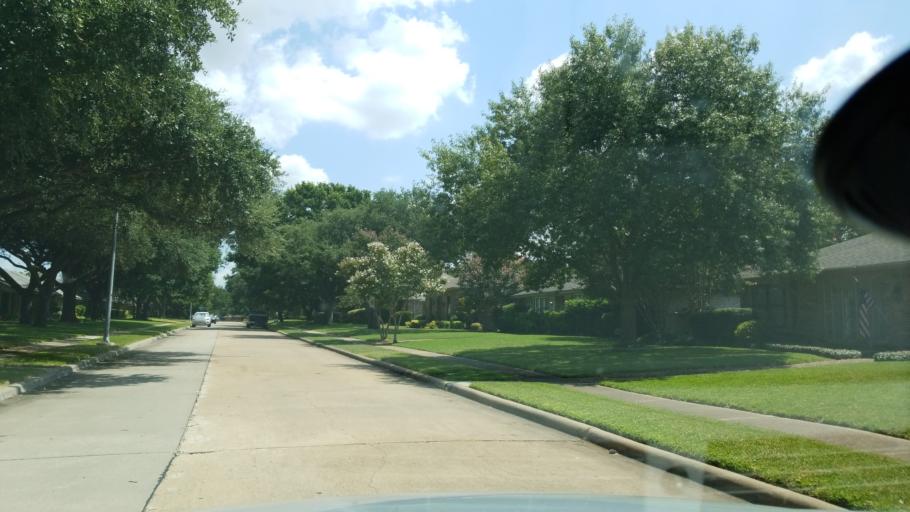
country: US
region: Texas
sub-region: Dallas County
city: Richardson
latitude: 32.9302
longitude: -96.7230
